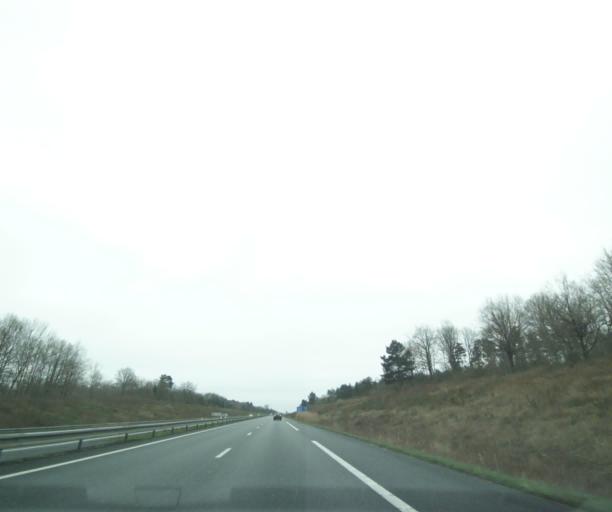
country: FR
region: Centre
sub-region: Departement du Loir-et-Cher
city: Lamotte-Beuvron
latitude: 47.5755
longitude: 1.9998
